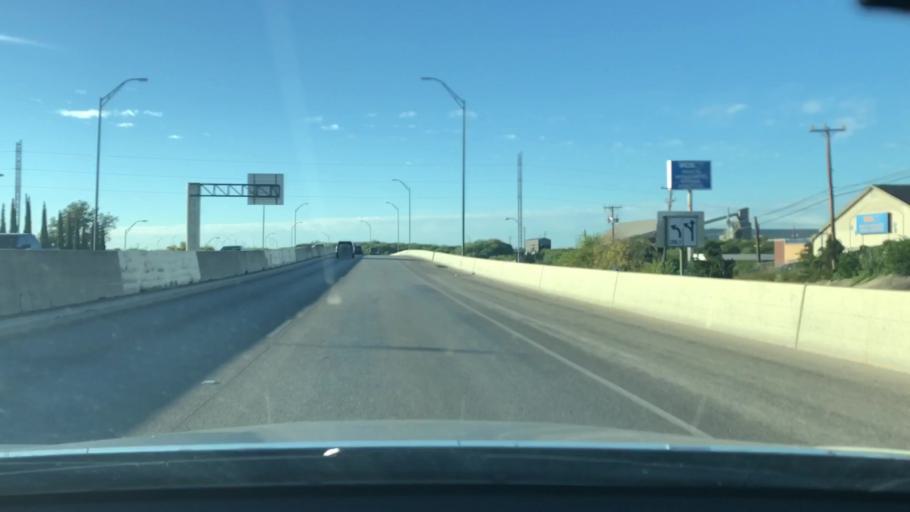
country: US
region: Texas
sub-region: Bexar County
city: Windcrest
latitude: 29.5398
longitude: -98.4199
